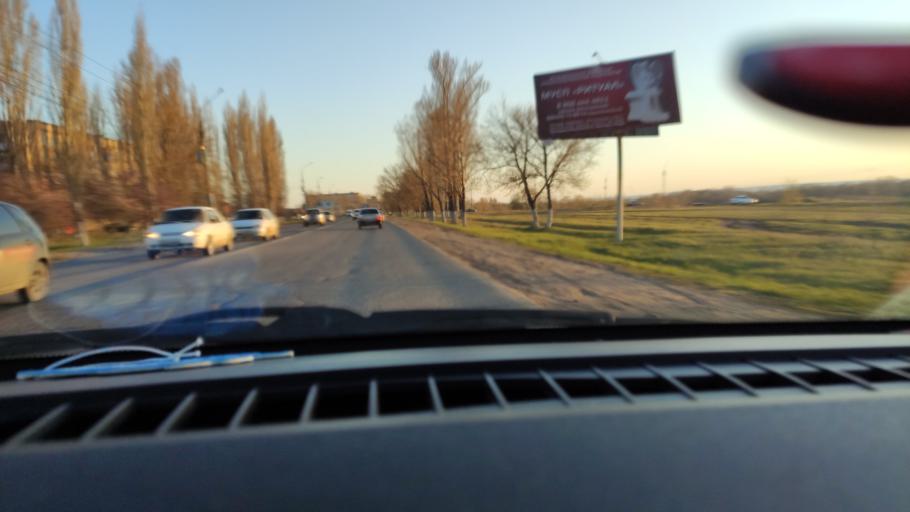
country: RU
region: Saratov
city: Engel's
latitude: 51.4516
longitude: 46.0829
